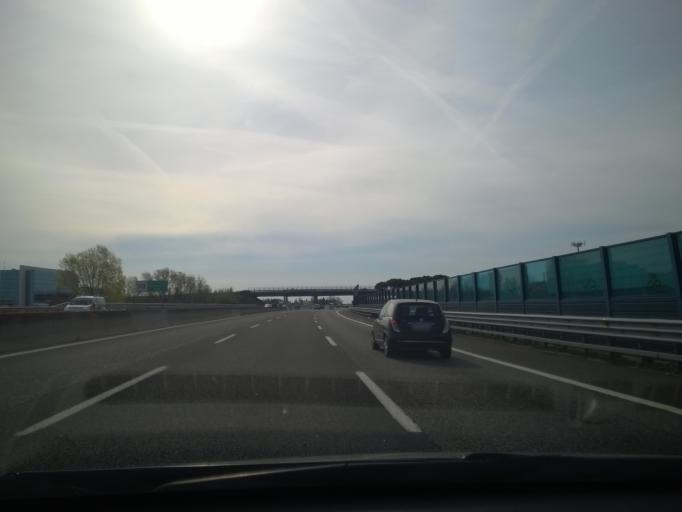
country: IT
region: Emilia-Romagna
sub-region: Forli-Cesena
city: San Mauro Pascoli
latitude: 44.1134
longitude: 12.4176
